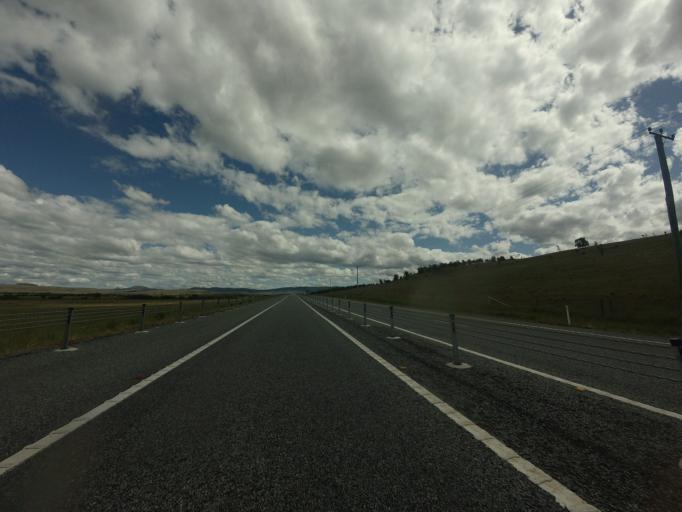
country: AU
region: Tasmania
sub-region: Northern Midlands
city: Evandale
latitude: -42.1190
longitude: 147.4386
